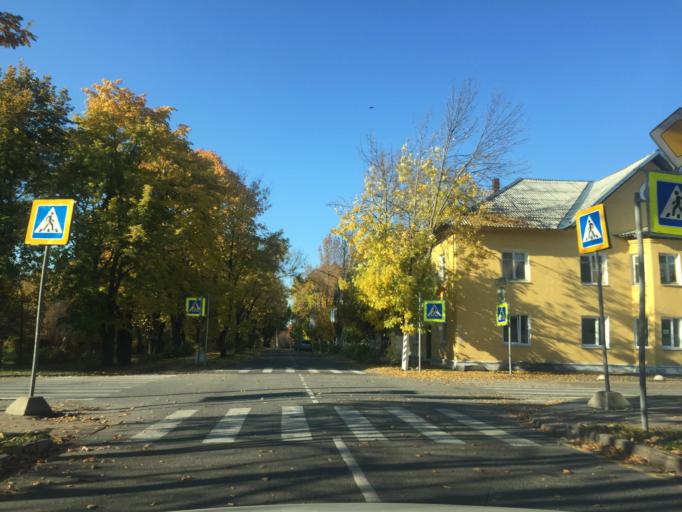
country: RU
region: Leningrad
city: Priozersk
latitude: 61.0358
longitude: 30.1122
